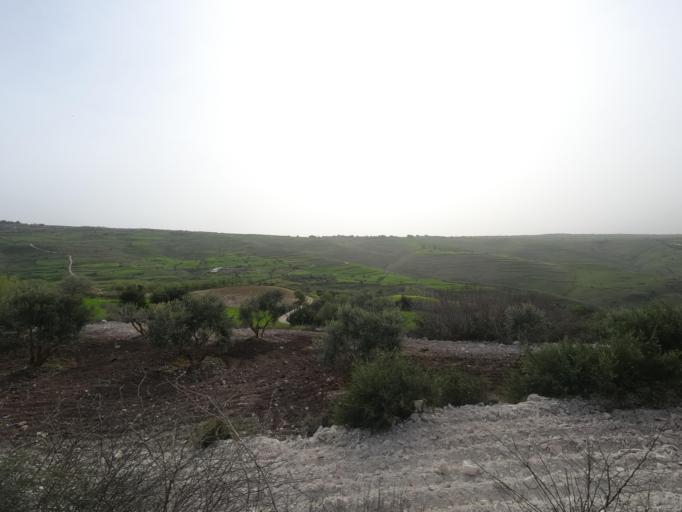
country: CY
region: Pafos
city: Pegeia
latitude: 34.9438
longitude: 32.3824
